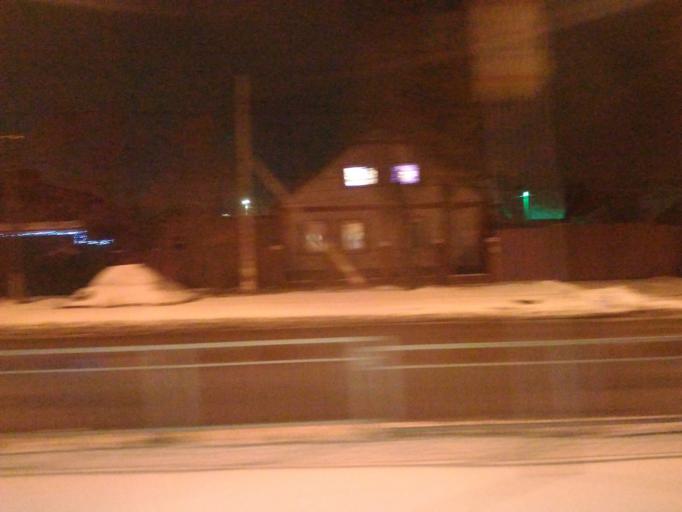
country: RU
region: Ulyanovsk
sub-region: Ulyanovskiy Rayon
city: Ulyanovsk
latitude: 54.3554
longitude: 48.3772
